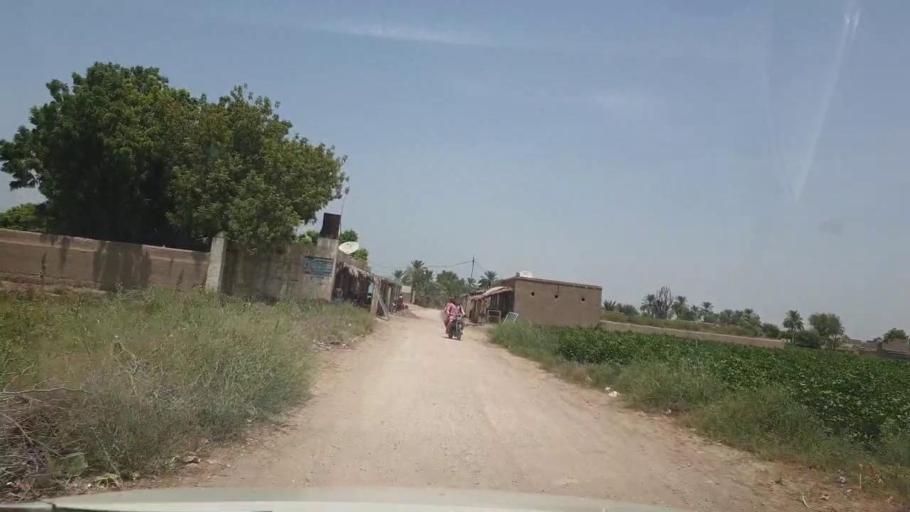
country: PK
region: Sindh
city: Bozdar
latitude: 27.1581
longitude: 68.6142
